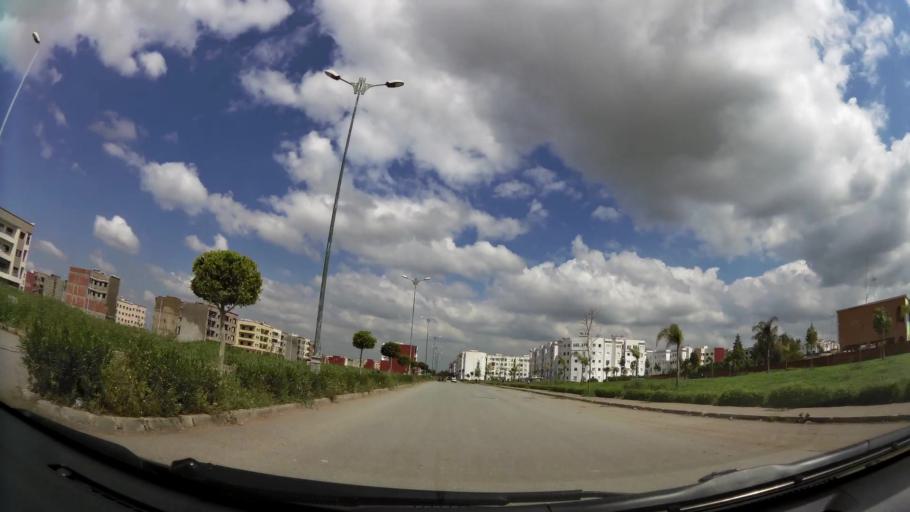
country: MA
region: Chaouia-Ouardigha
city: Nouaseur
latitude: 33.3618
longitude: -7.5450
